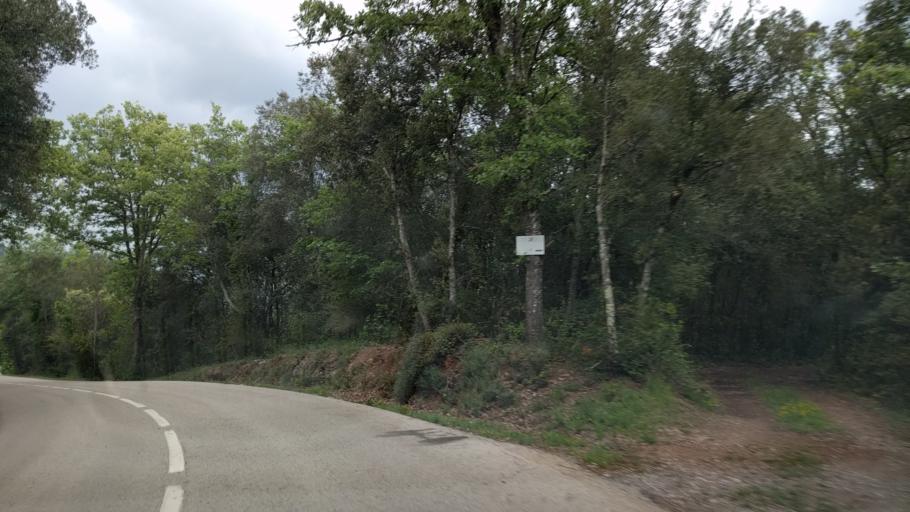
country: ES
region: Catalonia
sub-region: Provincia de Girona
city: la Cellera de Ter
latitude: 42.0227
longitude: 2.6688
